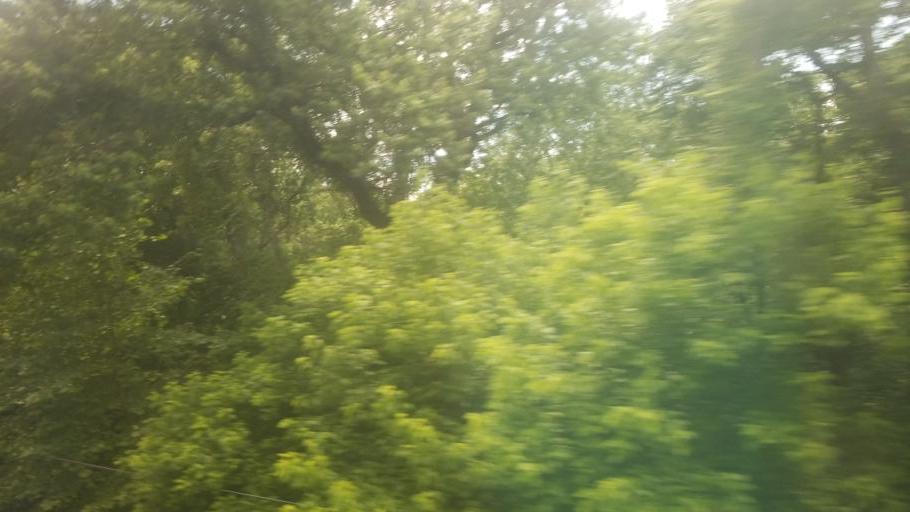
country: US
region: Maryland
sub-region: Frederick County
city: Brunswick
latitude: 39.3184
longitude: -77.6532
